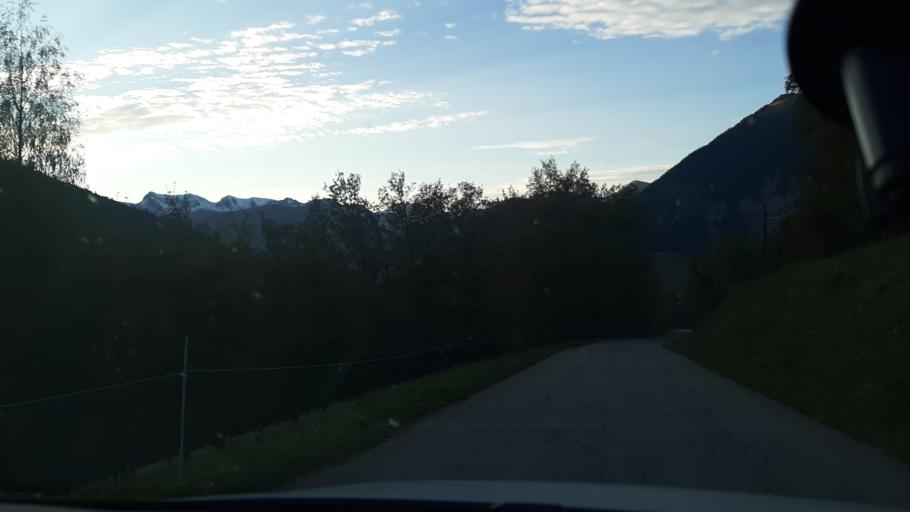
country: FR
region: Rhone-Alpes
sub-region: Departement de la Savoie
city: Villargondran
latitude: 45.1890
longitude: 6.3135
